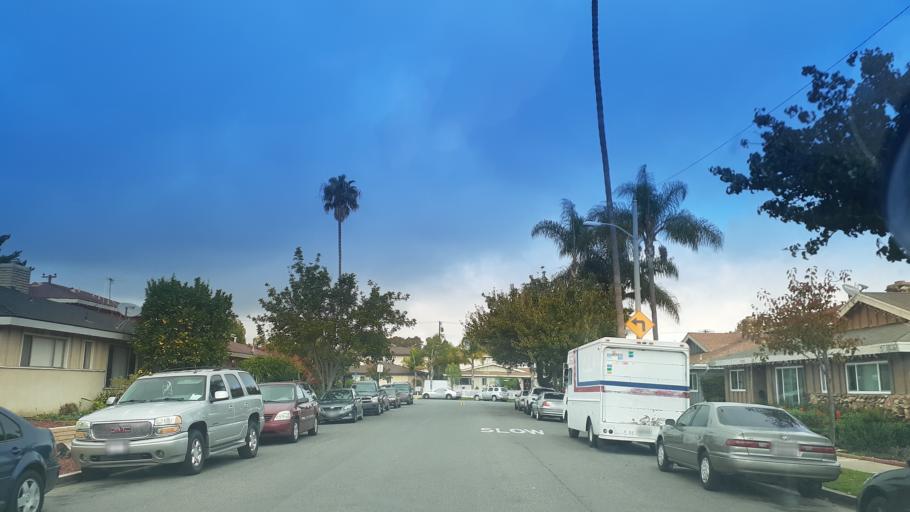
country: US
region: California
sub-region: Orange County
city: Costa Mesa
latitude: 33.6568
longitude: -117.9217
